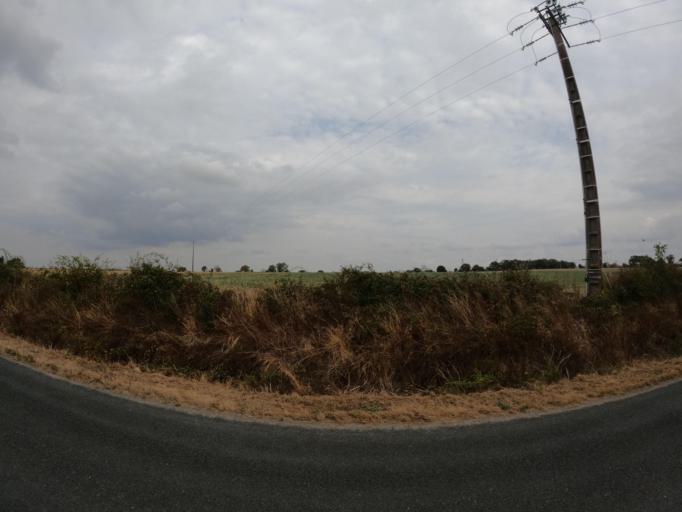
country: FR
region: Pays de la Loire
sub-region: Departement de la Vendee
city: Les Landes-Genusson
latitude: 46.9848
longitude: -1.1102
